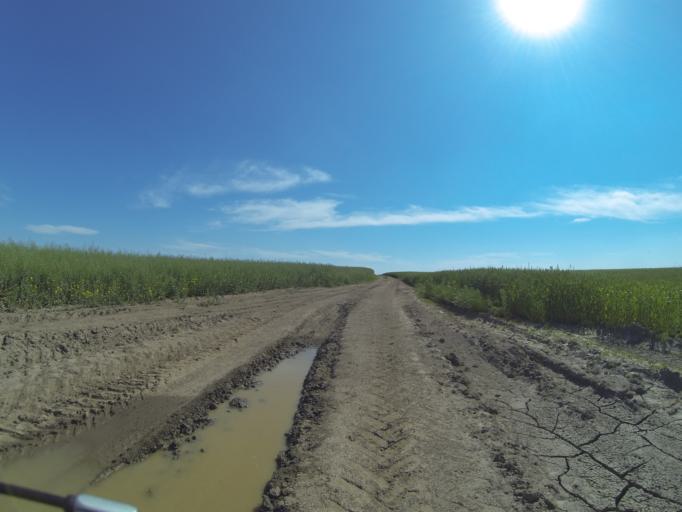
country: RO
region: Dolj
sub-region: Comuna Cosoveni
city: Cosoveni
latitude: 44.2590
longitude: 24.0000
